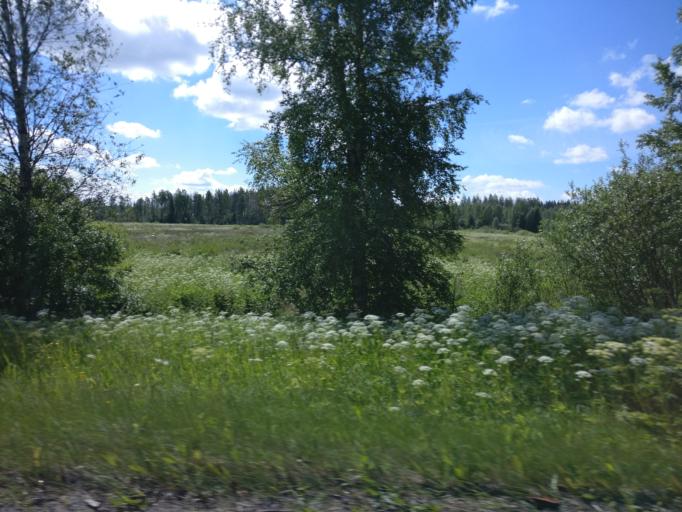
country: FI
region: Southern Savonia
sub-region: Savonlinna
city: Savonlinna
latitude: 61.8772
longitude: 28.9879
